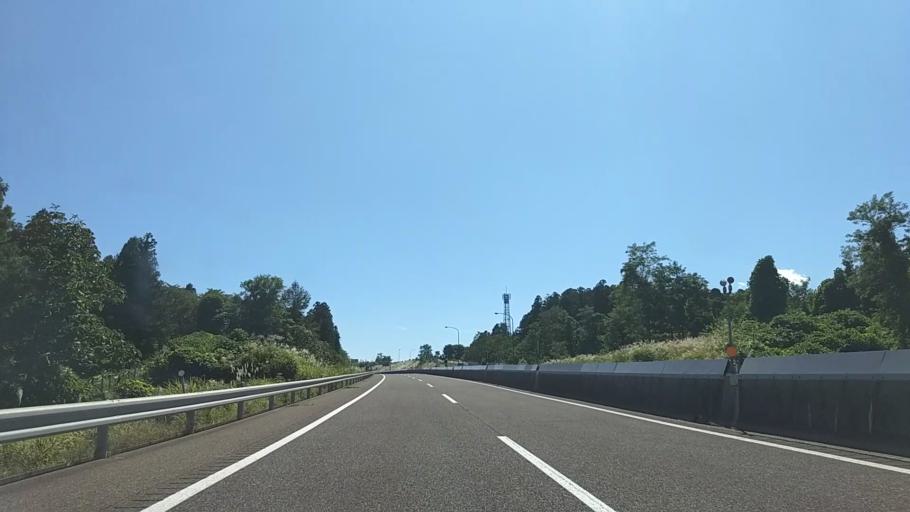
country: JP
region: Niigata
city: Arai
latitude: 36.9351
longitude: 138.2119
